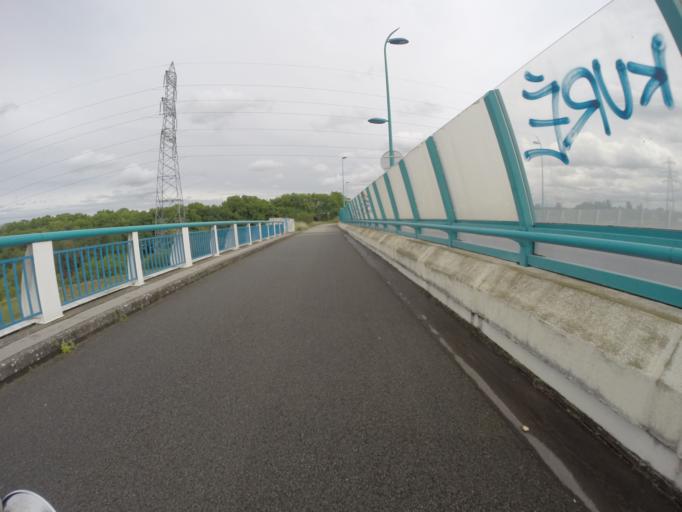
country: FR
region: Rhone-Alpes
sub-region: Departement du Rhone
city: Vaulx-en-Velin
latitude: 45.7708
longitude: 4.9327
